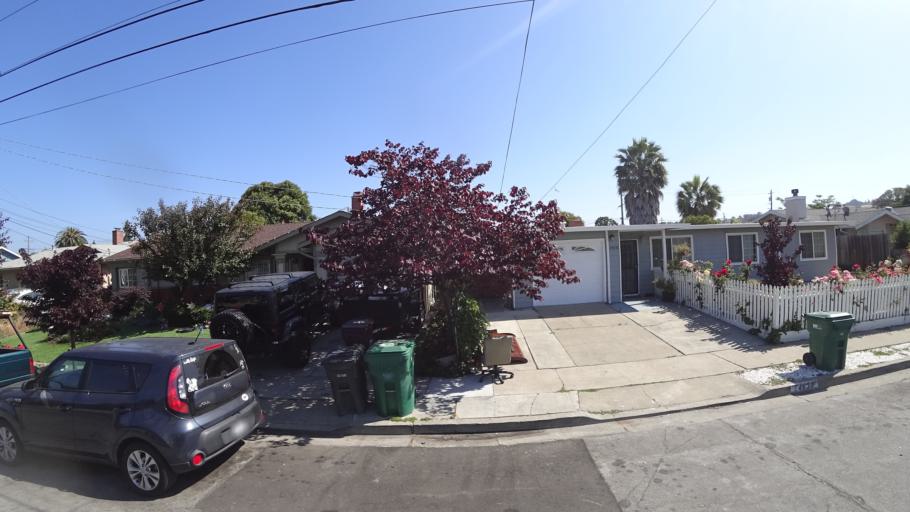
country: US
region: California
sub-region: Alameda County
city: Hayward
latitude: 37.6588
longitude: -122.0846
